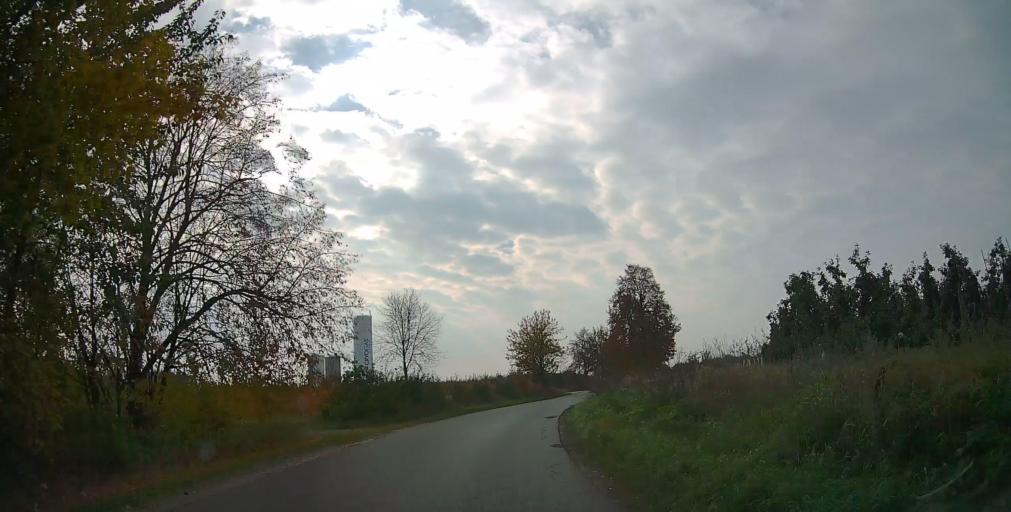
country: PL
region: Masovian Voivodeship
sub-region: Powiat grojecki
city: Mogielnica
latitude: 51.6806
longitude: 20.7144
